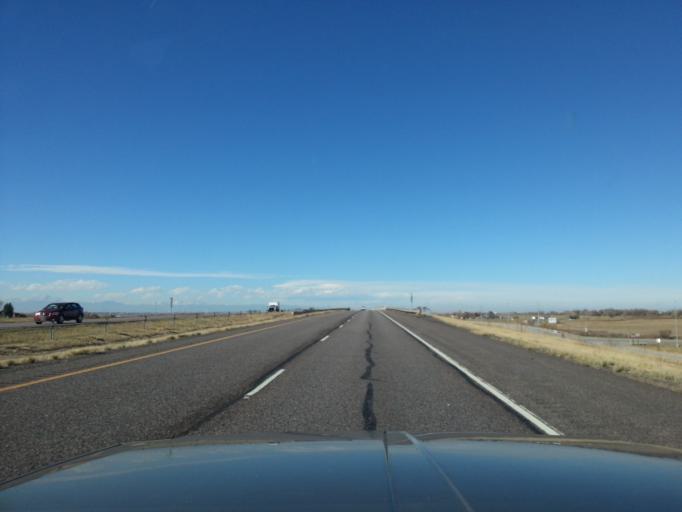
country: US
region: Colorado
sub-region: Adams County
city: Brighton
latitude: 39.9125
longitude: -104.7804
